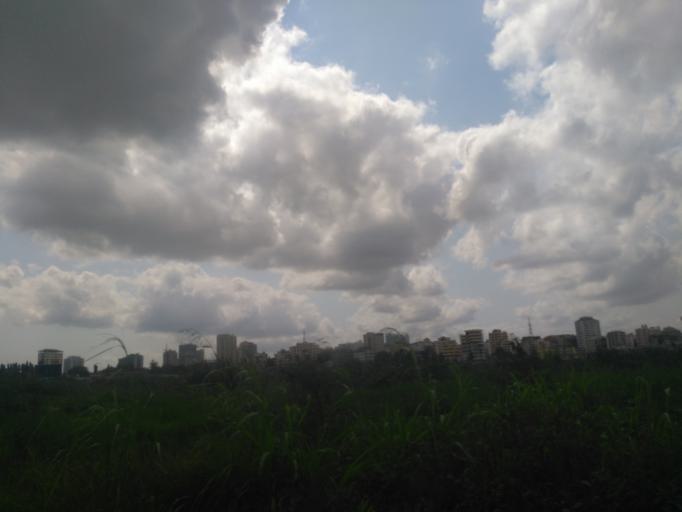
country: TZ
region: Dar es Salaam
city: Dar es Salaam
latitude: -6.8118
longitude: 39.2672
